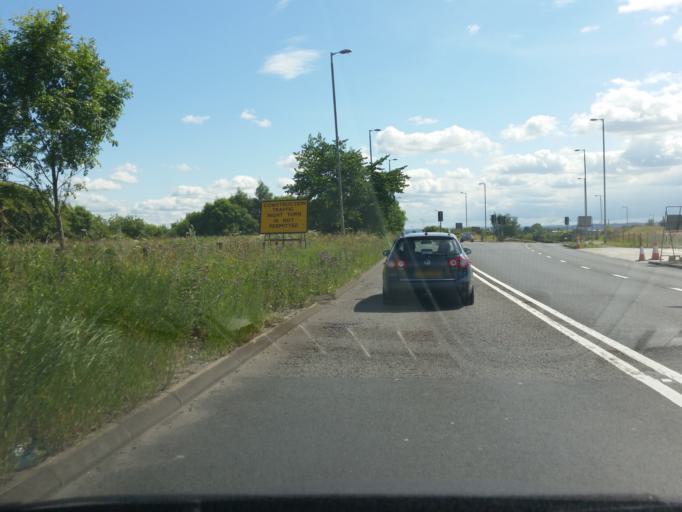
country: GB
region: Scotland
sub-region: North Lanarkshire
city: Bellshill
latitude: 55.8379
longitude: -4.0248
